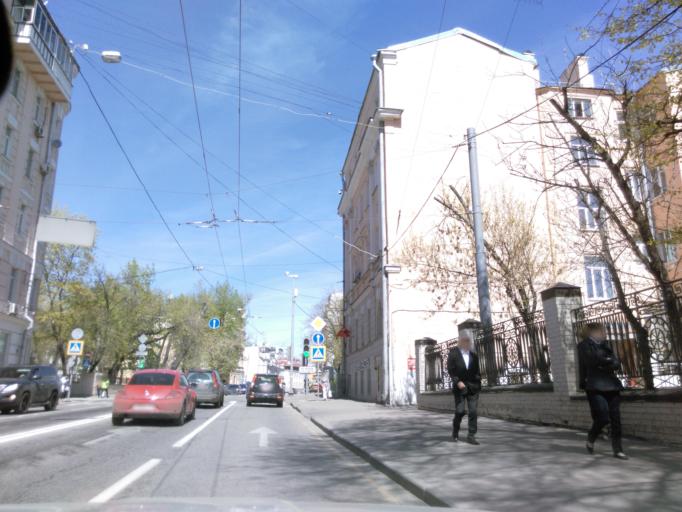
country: RU
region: Moscow
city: Moscow
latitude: 55.7377
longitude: 37.5953
